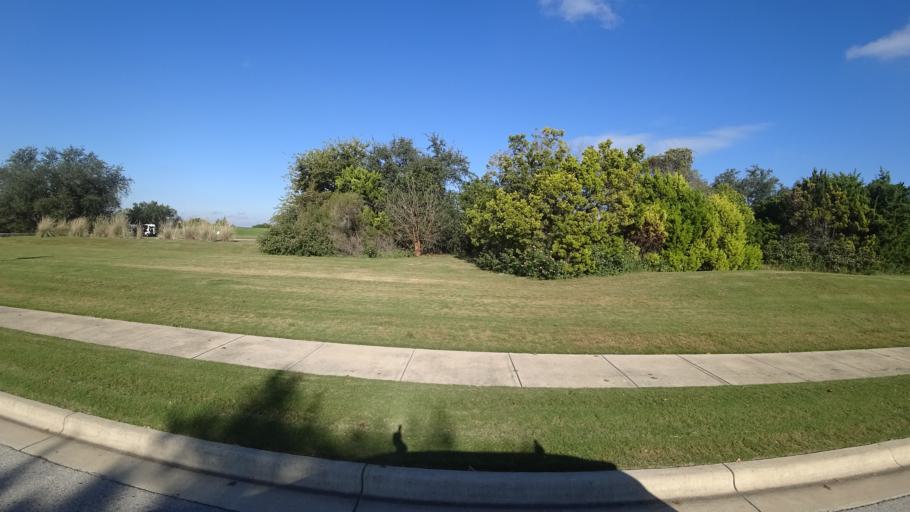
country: US
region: Texas
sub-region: Travis County
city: Hudson Bend
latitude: 30.3571
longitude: -97.8907
